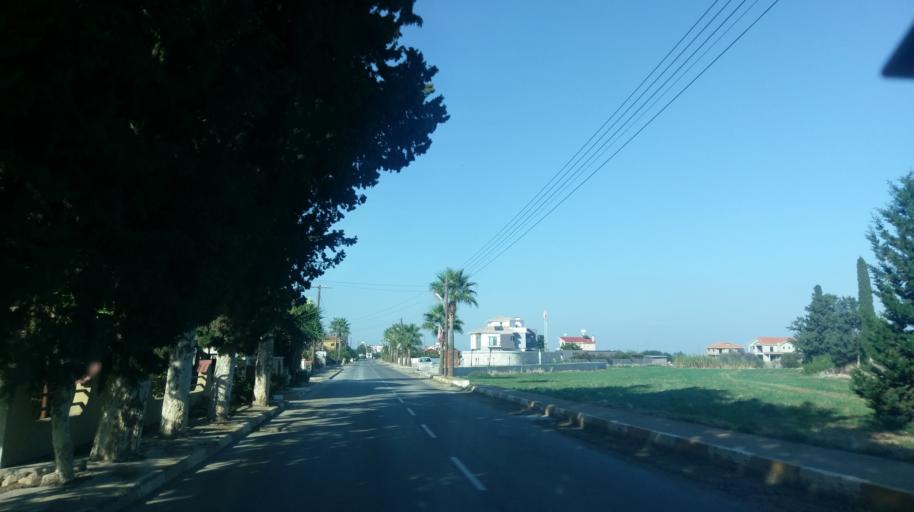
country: CY
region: Larnaka
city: Pergamos
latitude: 35.0470
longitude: 33.7092
